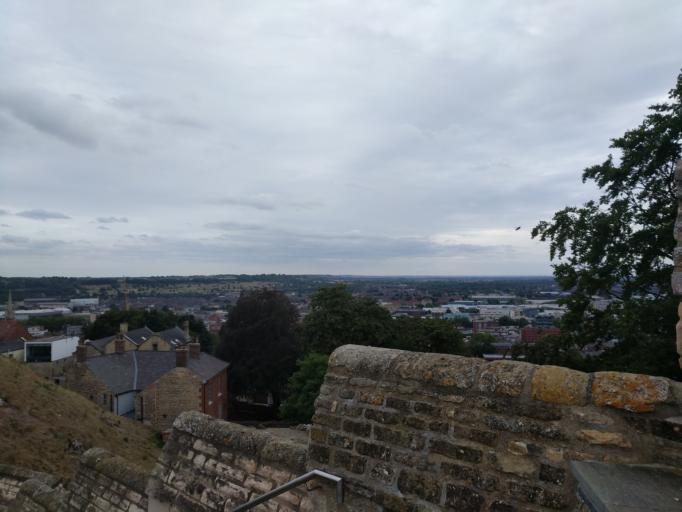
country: GB
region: England
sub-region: Lincolnshire
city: Lincoln
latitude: 53.2346
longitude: -0.5424
